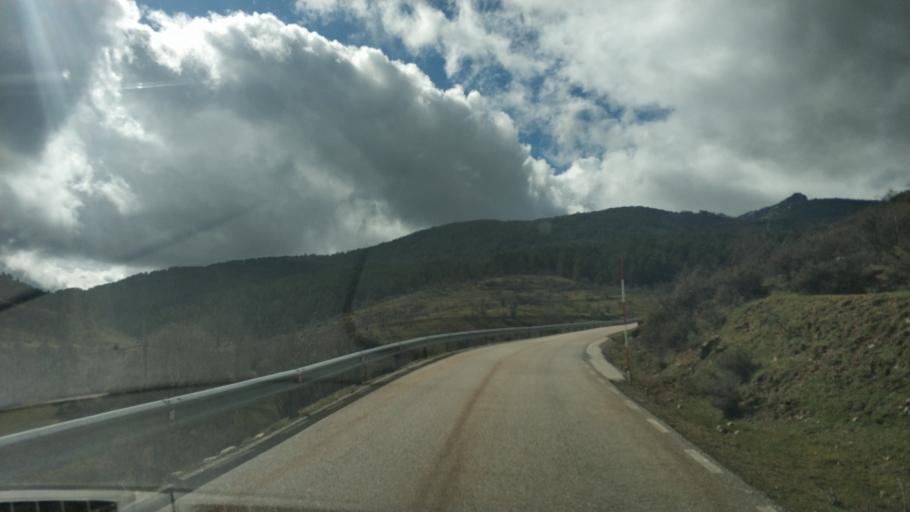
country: ES
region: Castille and Leon
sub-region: Provincia de Burgos
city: Neila
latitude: 42.0573
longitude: -3.0061
